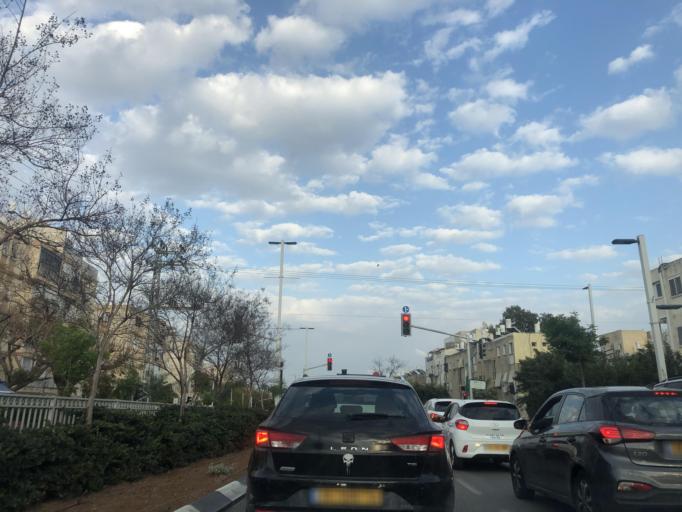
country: IL
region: Tel Aviv
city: Bat Yam
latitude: 32.0233
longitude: 34.7577
